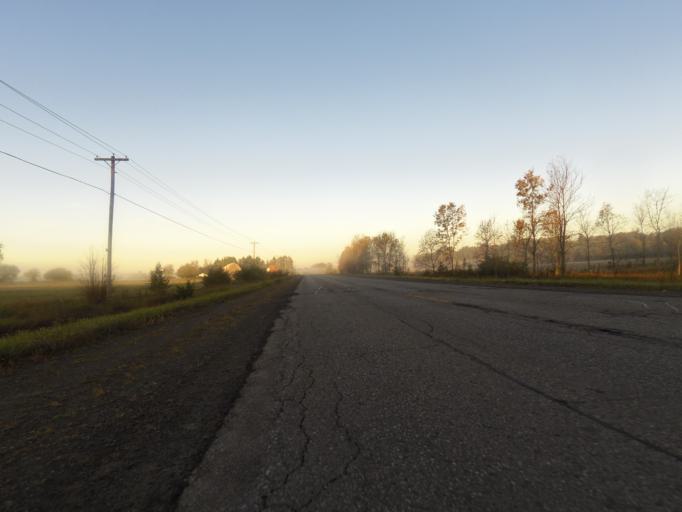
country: CA
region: Ontario
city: Quinte West
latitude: 44.0405
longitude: -77.6113
